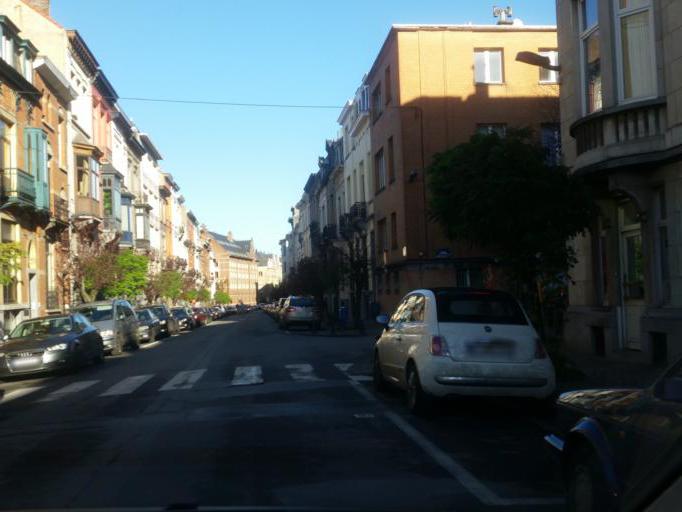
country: BE
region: Brussels Capital
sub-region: Bruxelles-Capitale
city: Brussels
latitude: 50.8206
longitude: 4.3543
